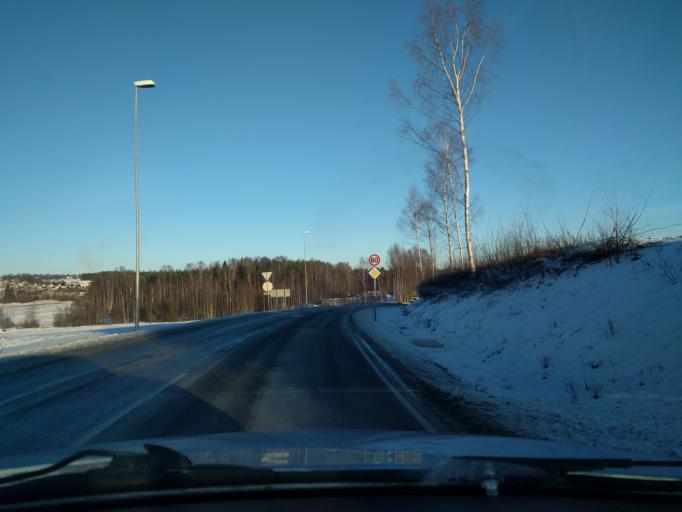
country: NO
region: Hedmark
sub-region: Hamar
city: Hamar
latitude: 60.7871
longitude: 11.1302
